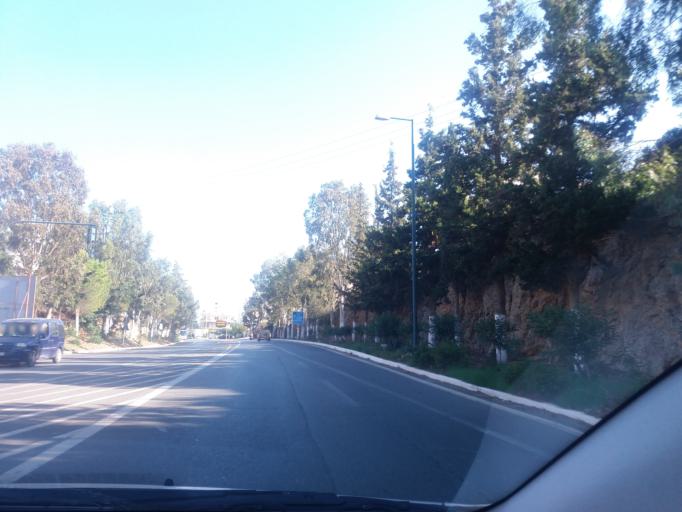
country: GR
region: Crete
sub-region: Nomos Lasithiou
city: Agios Nikolaos
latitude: 35.1989
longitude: 25.7075
